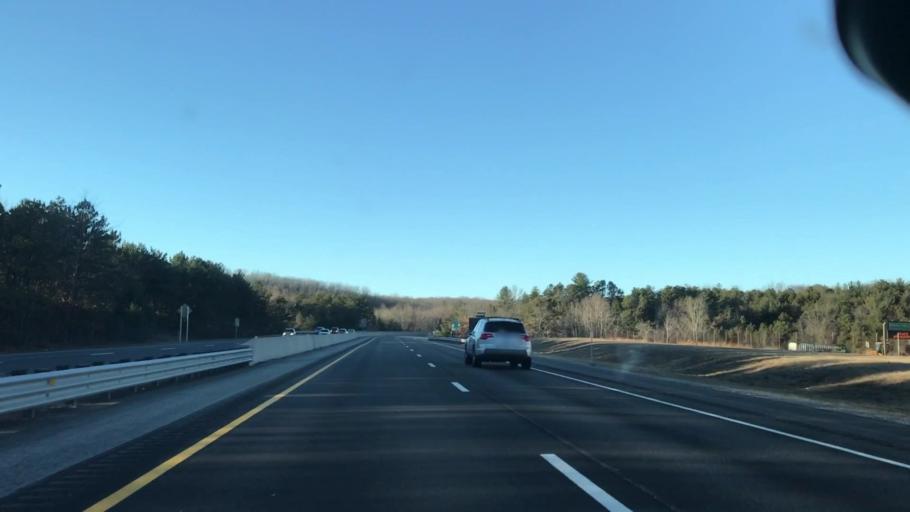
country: US
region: New Hampshire
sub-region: Hillsborough County
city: Pinardville
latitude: 43.0182
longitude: -71.4847
